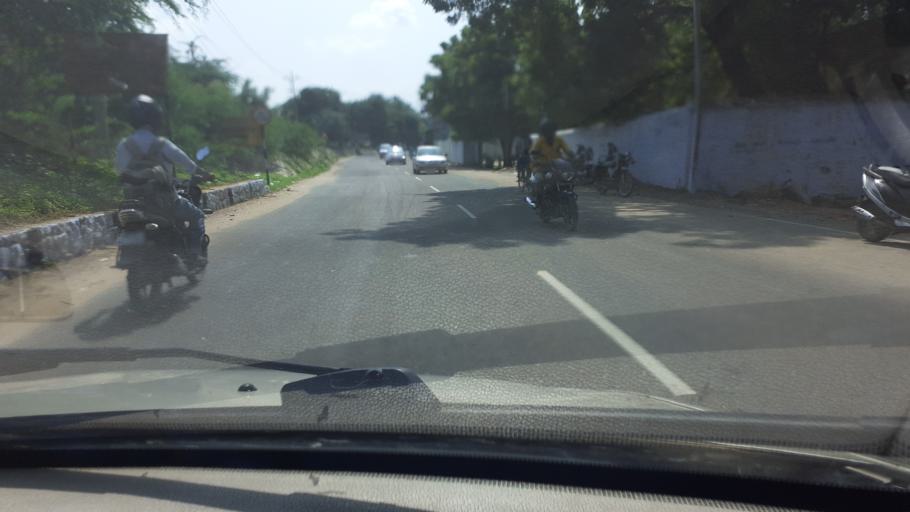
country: IN
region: Tamil Nadu
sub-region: Thoothukkudi
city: Srivaikuntam
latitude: 8.6257
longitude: 77.9081
